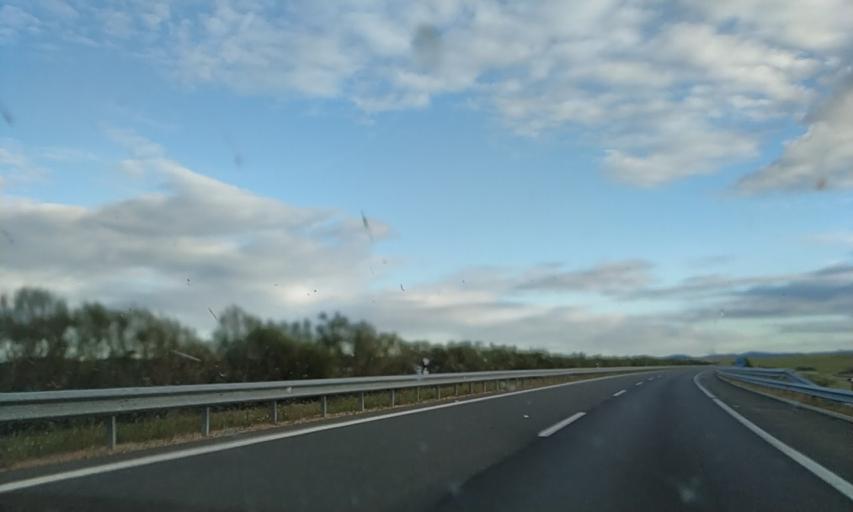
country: ES
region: Extremadura
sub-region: Provincia de Caceres
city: Caceres
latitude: 39.4901
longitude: -6.4366
